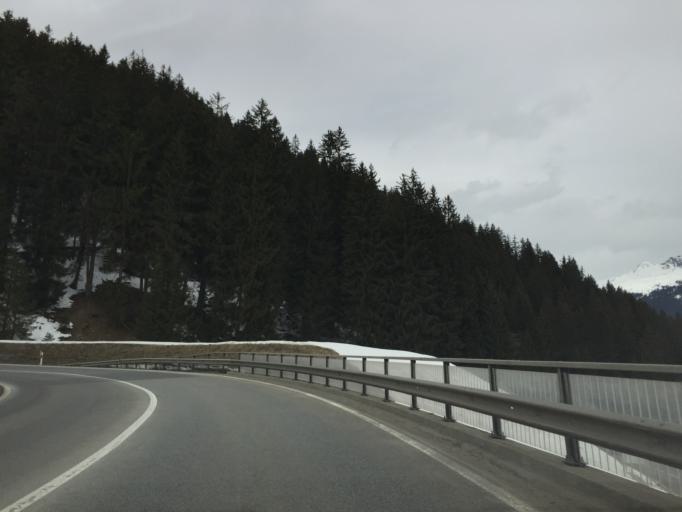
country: CH
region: Grisons
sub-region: Praettigau/Davos District
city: Klosters Serneus
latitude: 46.8599
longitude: 9.8791
